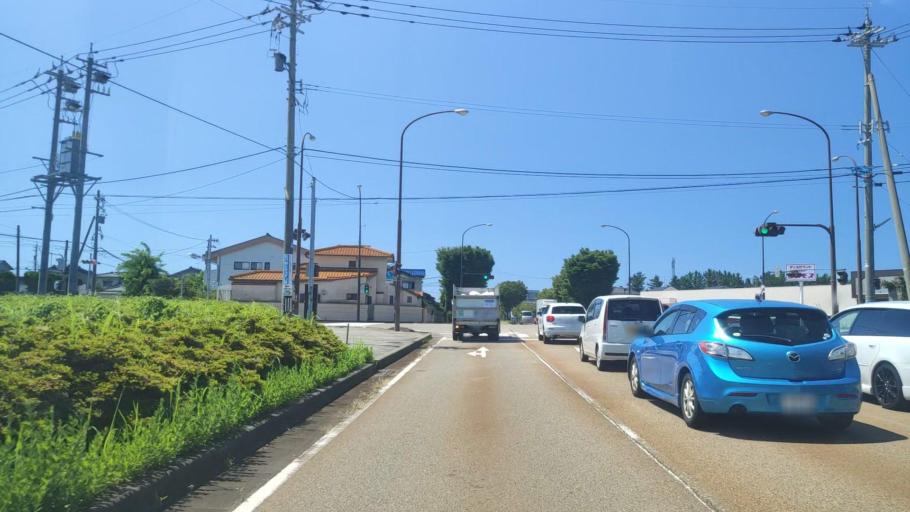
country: JP
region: Ishikawa
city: Kanazawa-shi
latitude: 36.6314
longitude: 136.6271
